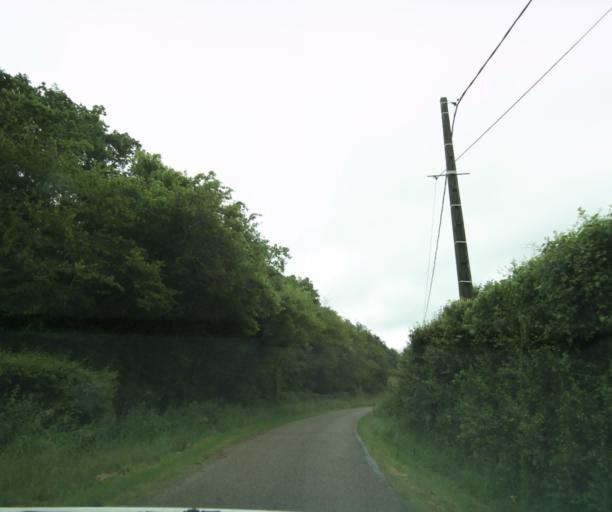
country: FR
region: Bourgogne
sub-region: Departement de Saone-et-Loire
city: Charolles
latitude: 46.5040
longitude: 4.2904
